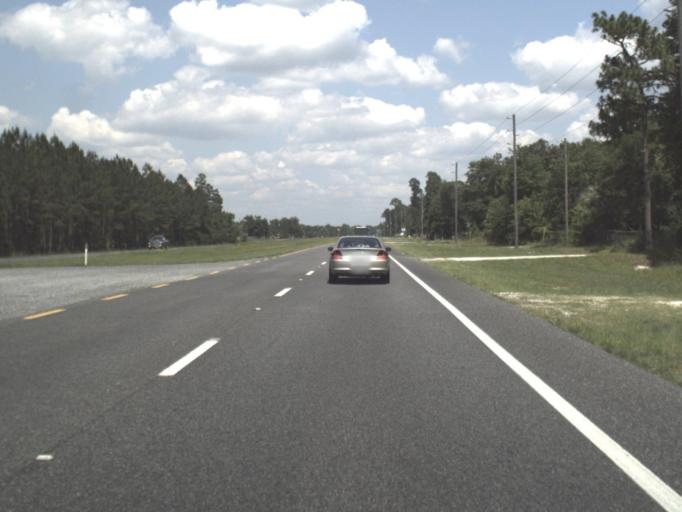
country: US
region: Florida
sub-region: Alachua County
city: Hawthorne
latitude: 29.5978
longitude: -82.1138
